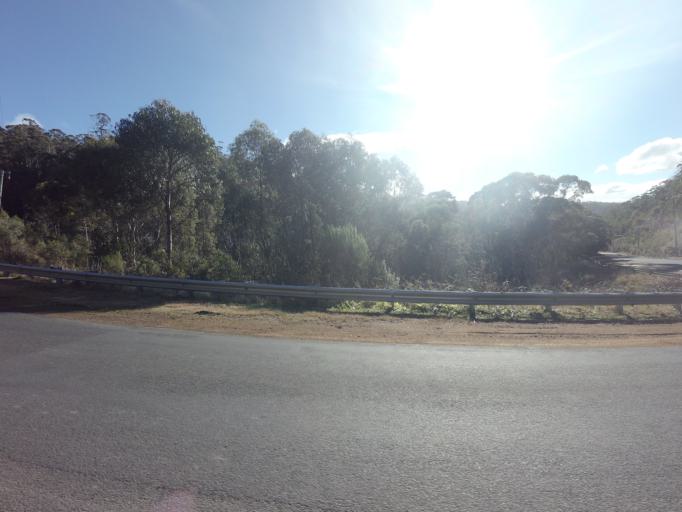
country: AU
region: Tasmania
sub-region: Glenorchy
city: Berriedale
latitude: -42.8265
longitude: 147.2086
